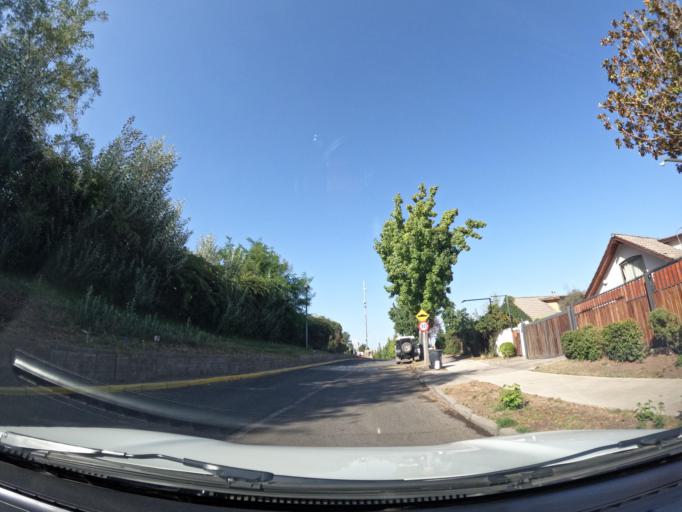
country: CL
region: Santiago Metropolitan
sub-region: Provincia de Santiago
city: Villa Presidente Frei, Nunoa, Santiago, Chile
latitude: -33.4858
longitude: -70.5380
